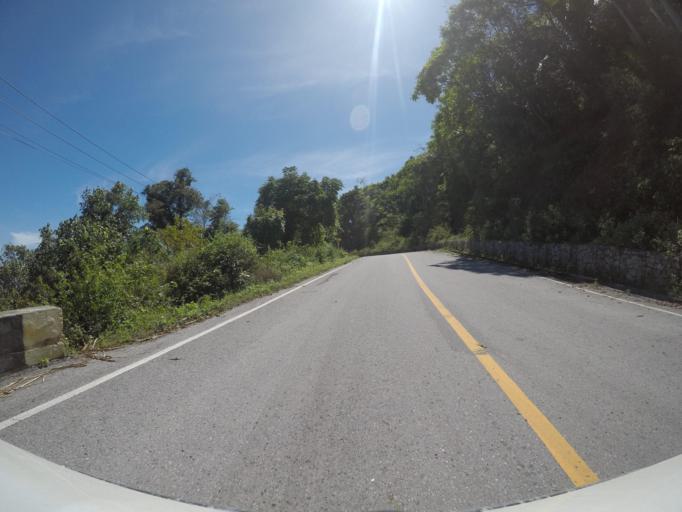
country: TL
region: Manufahi
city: Same
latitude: -8.8997
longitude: 125.9795
